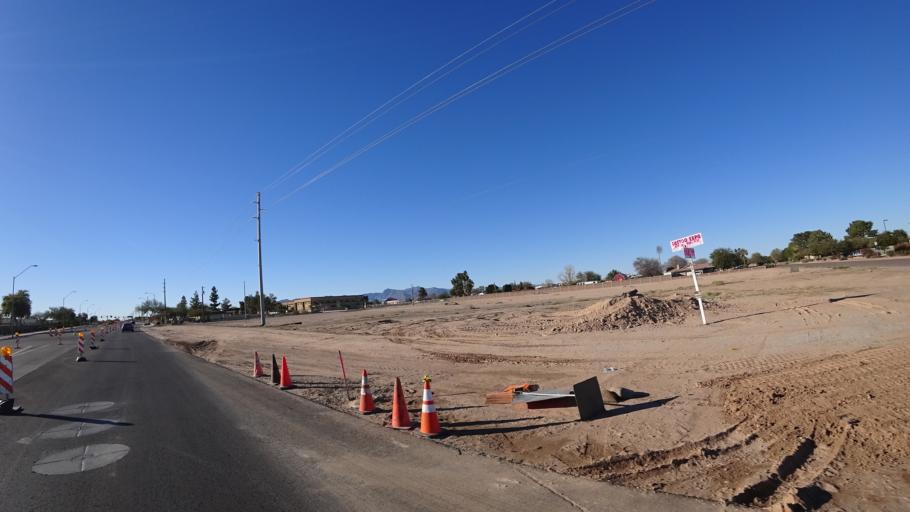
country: US
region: Arizona
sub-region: Maricopa County
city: Goodyear
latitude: 33.4501
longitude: -112.4055
